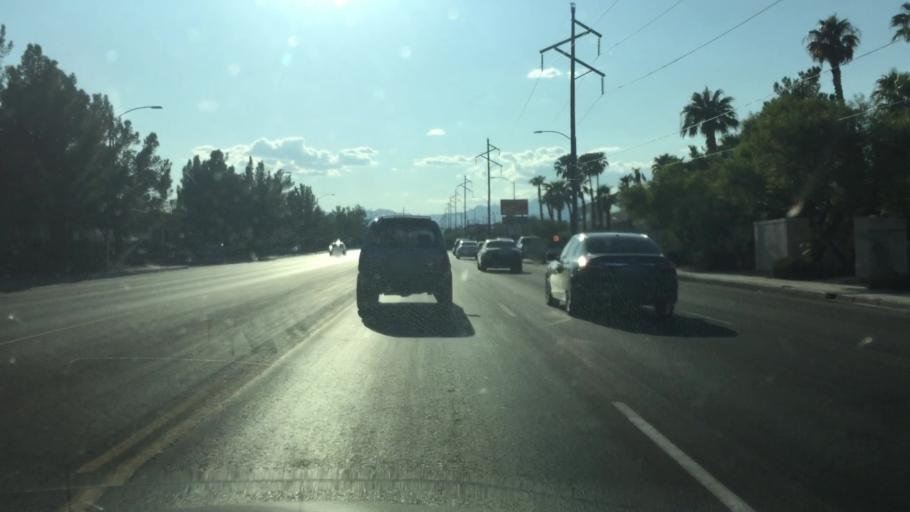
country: US
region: Nevada
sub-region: Clark County
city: Spring Valley
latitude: 36.1591
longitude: -115.2677
